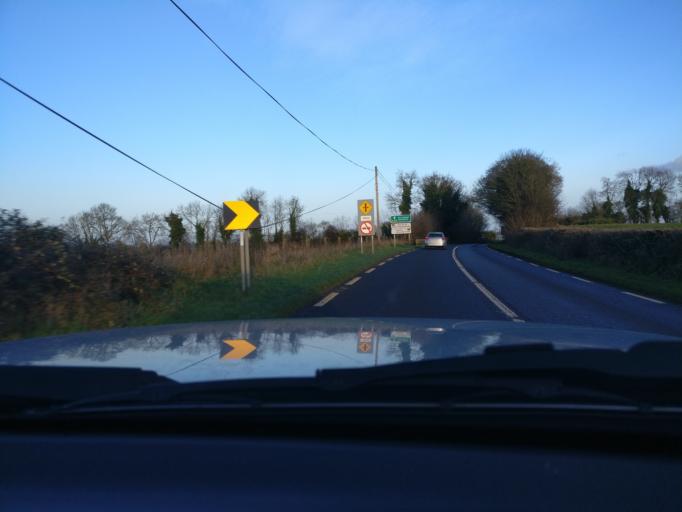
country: IE
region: Leinster
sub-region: Lu
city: Ardee
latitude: 53.8432
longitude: -6.6076
